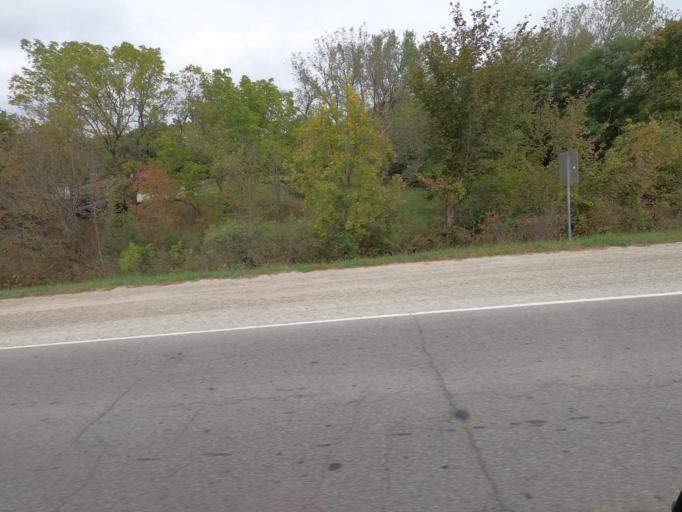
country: US
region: Iowa
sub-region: Wapello County
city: Ottumwa
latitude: 40.9220
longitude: -92.2290
